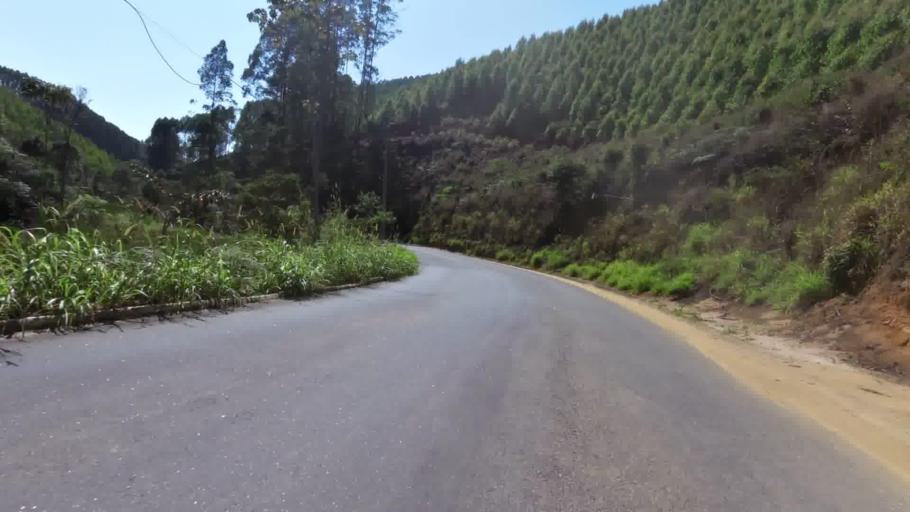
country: BR
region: Espirito Santo
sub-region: Marechal Floriano
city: Marechal Floriano
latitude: -20.4396
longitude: -40.8819
